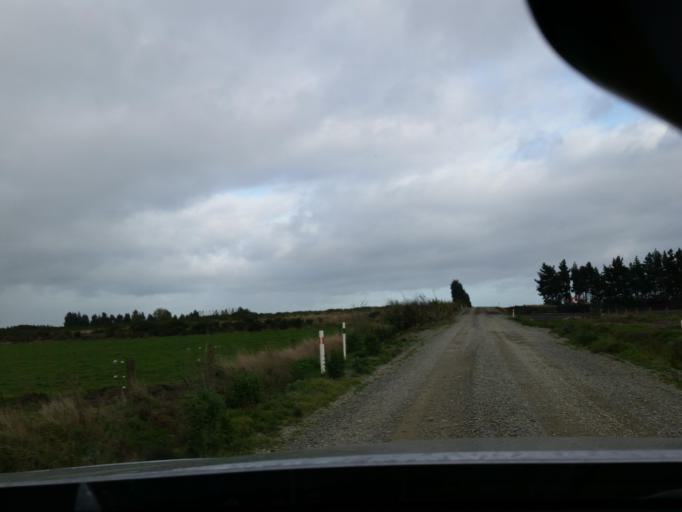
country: NZ
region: Southland
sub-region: Southland District
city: Winton
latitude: -46.2369
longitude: 168.3672
